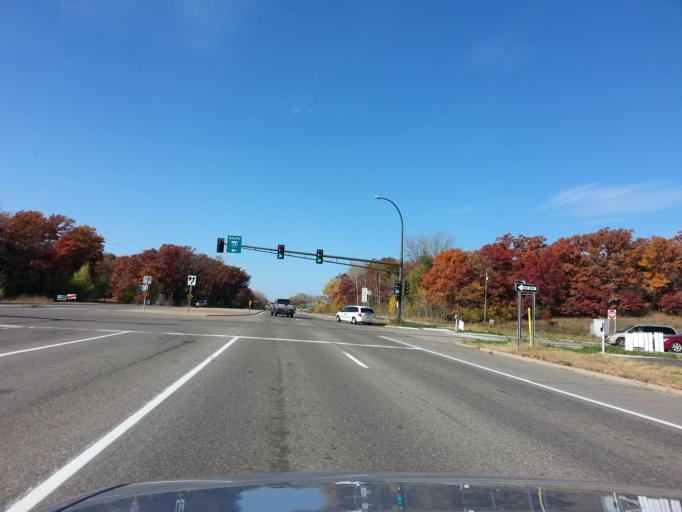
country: US
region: Minnesota
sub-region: Dakota County
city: Lakeville
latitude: 44.6814
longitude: -93.2939
